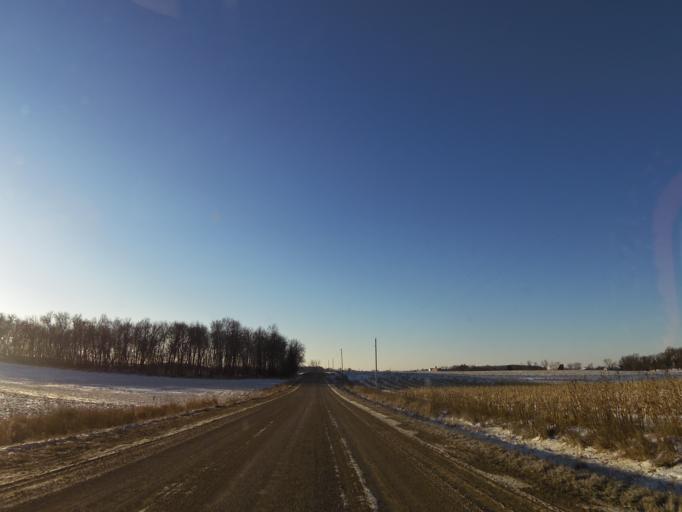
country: US
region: Minnesota
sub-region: Scott County
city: Jordan
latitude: 44.6686
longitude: -93.5419
